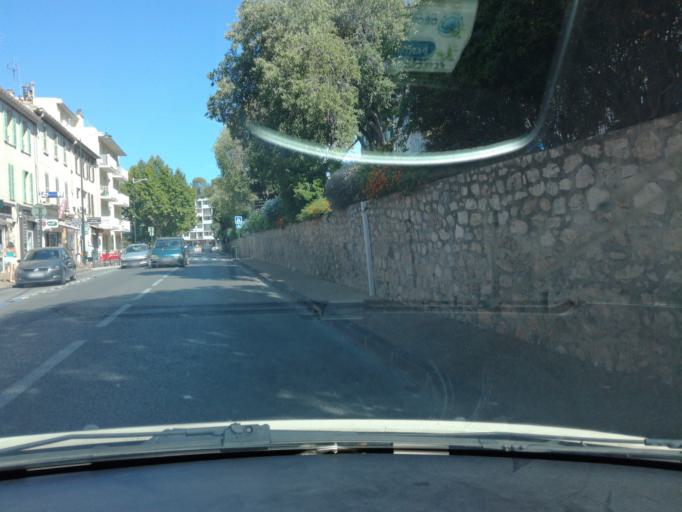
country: FR
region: Provence-Alpes-Cote d'Azur
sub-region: Departement du Var
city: Hyeres
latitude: 43.1212
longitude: 6.1207
